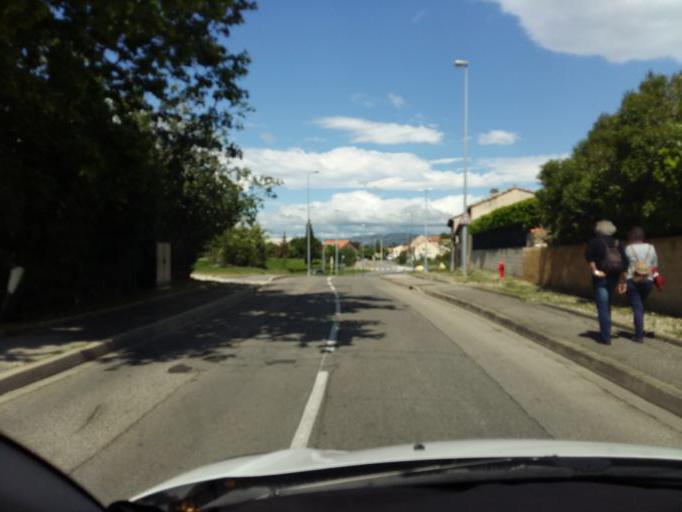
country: FR
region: Provence-Alpes-Cote d'Azur
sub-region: Departement du Vaucluse
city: Cavaillon
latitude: 43.8433
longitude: 5.0440
